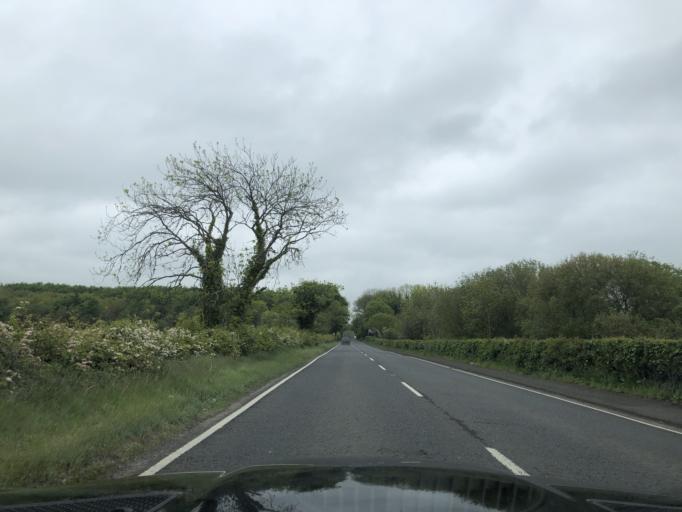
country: GB
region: Northern Ireland
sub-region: Down District
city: Downpatrick
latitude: 54.3135
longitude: -5.7363
